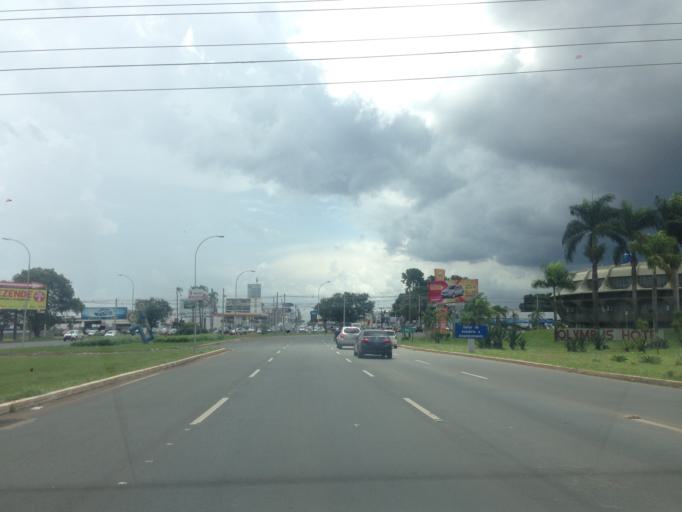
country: BR
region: Federal District
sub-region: Brasilia
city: Brasilia
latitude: -15.8077
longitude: -47.9499
